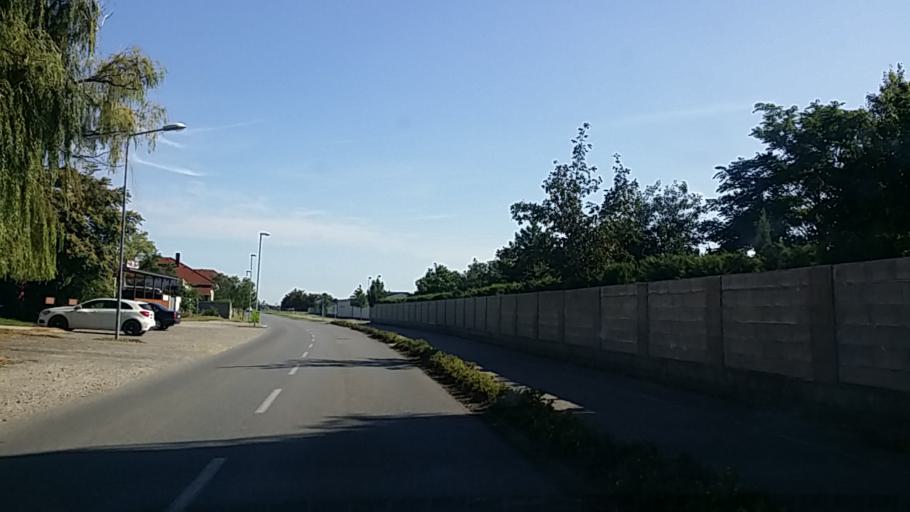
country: AT
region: Burgenland
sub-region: Politischer Bezirk Neusiedl am See
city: Apetlon
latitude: 47.7405
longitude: 16.8322
